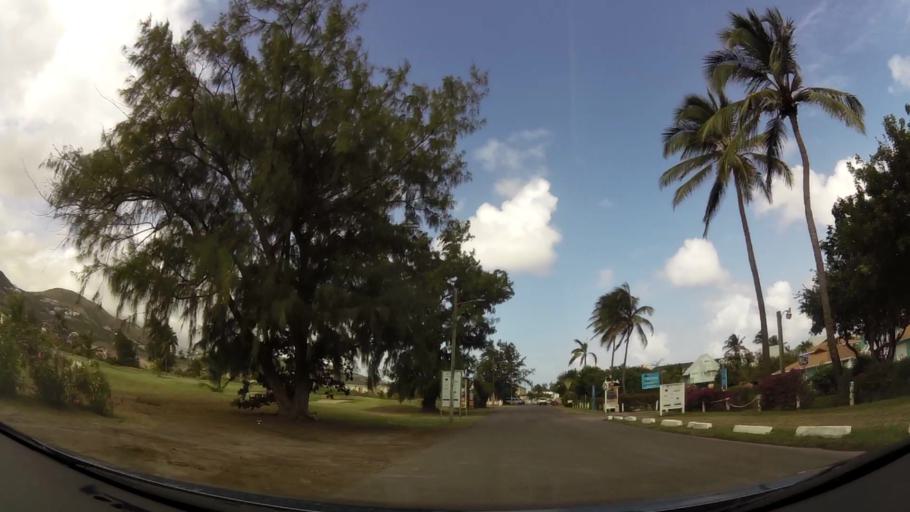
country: KN
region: Saint George Basseterre
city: Basseterre
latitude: 17.2871
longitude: -62.6859
